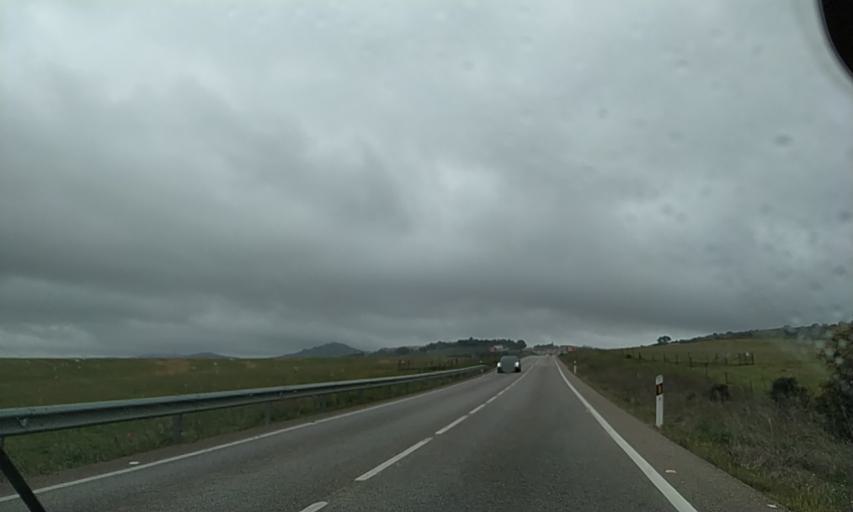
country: ES
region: Extremadura
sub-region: Provincia de Caceres
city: Caceres
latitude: 39.4970
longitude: -6.3869
